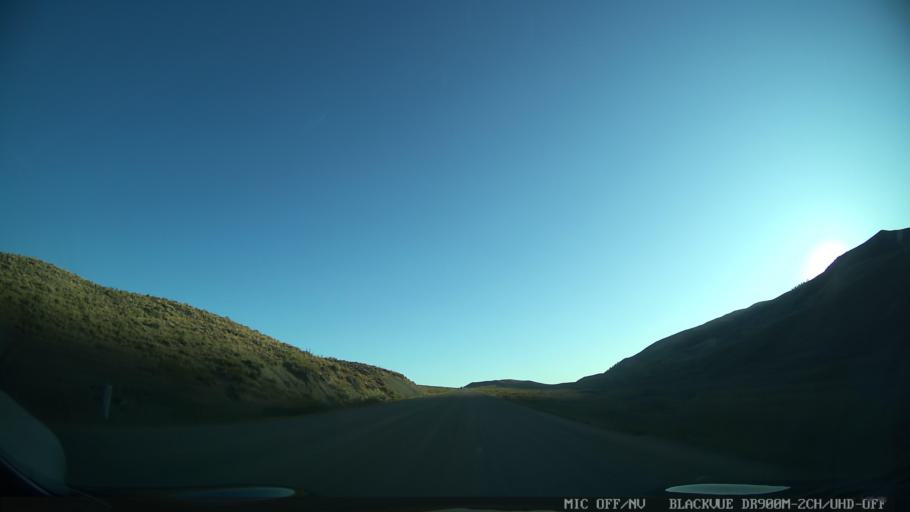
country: US
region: Colorado
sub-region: Grand County
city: Kremmling
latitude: 40.0324
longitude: -106.3812
